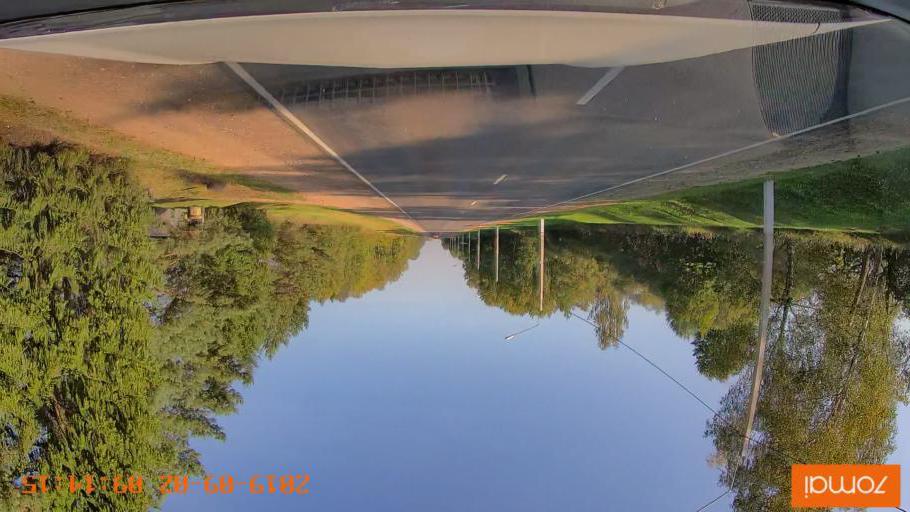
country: RU
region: Kaluga
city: Nikola-Lenivets
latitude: 54.8477
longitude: 35.5187
